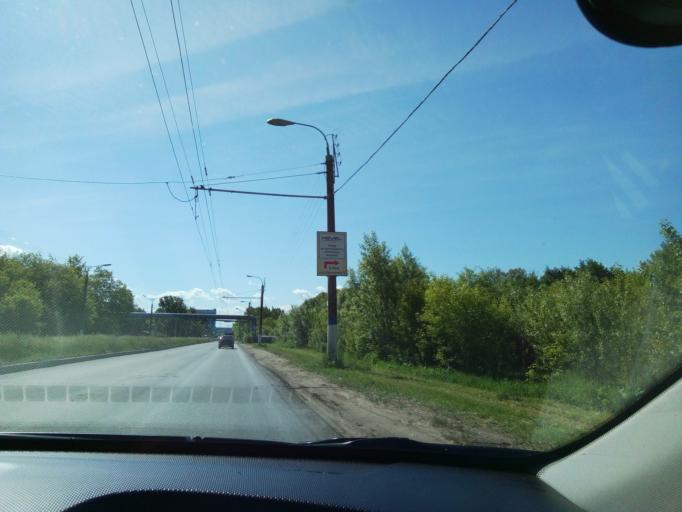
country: RU
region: Chuvashia
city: Novocheboksarsk
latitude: 56.0828
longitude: 47.5047
